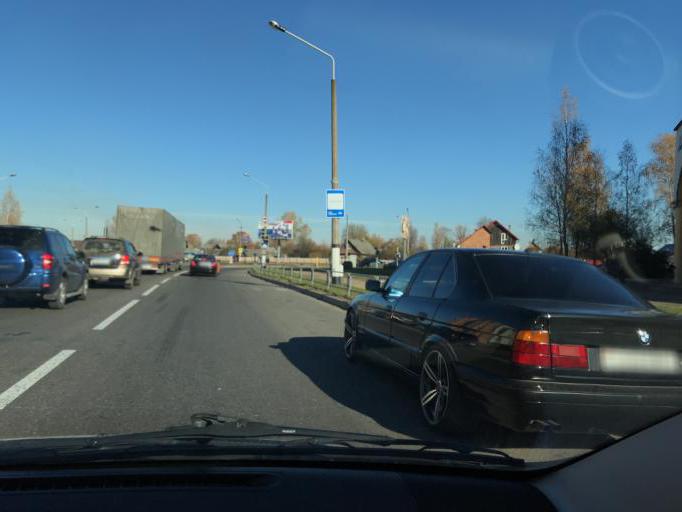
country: BY
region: Vitebsk
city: Polatsk
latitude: 55.4976
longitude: 28.7534
